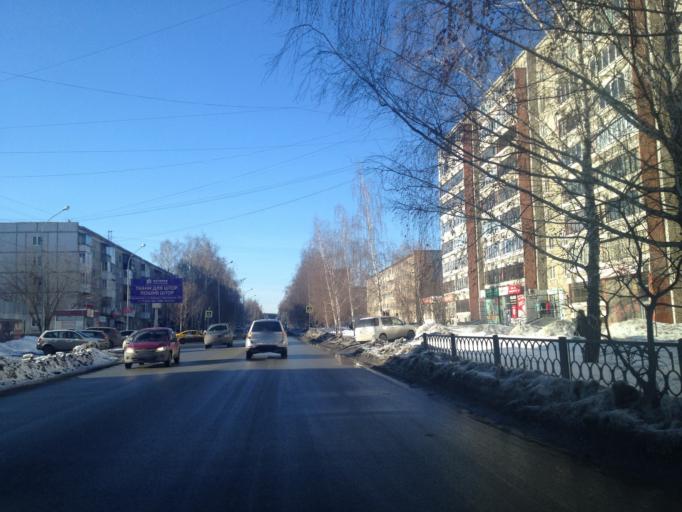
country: RU
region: Sverdlovsk
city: Sovkhoznyy
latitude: 56.8065
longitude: 60.5559
